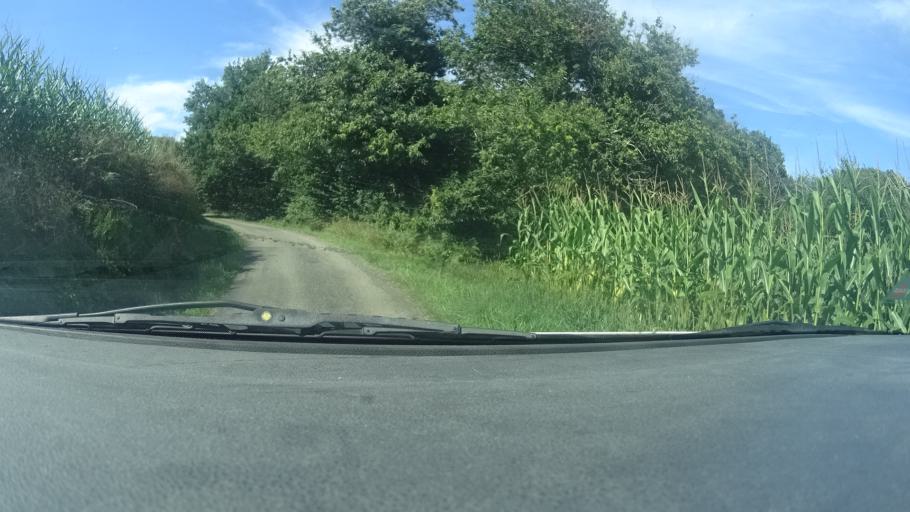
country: FR
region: Aquitaine
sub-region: Departement des Pyrenees-Atlantiques
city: Mont
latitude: 43.4979
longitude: -0.6895
